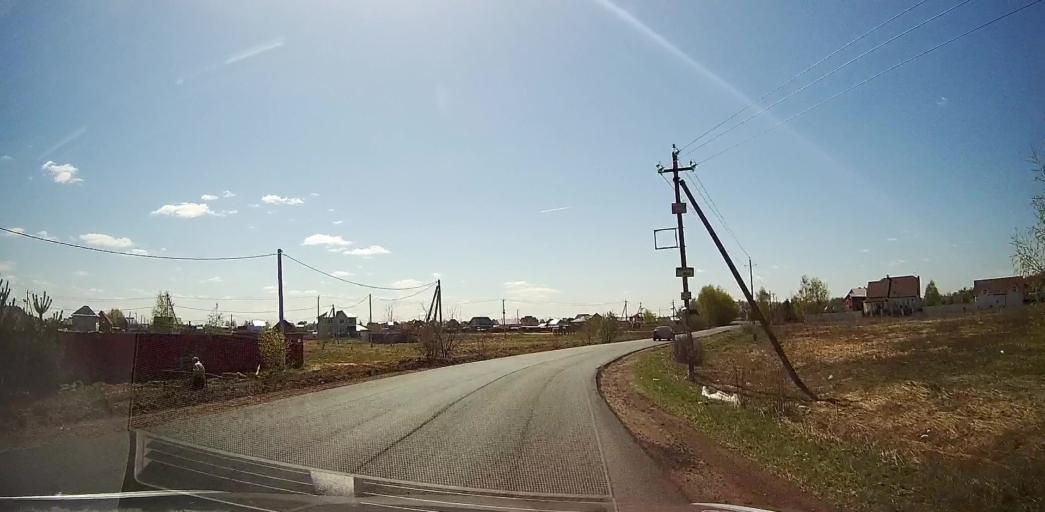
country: RU
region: Moskovskaya
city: Malyshevo
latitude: 55.4712
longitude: 38.3929
